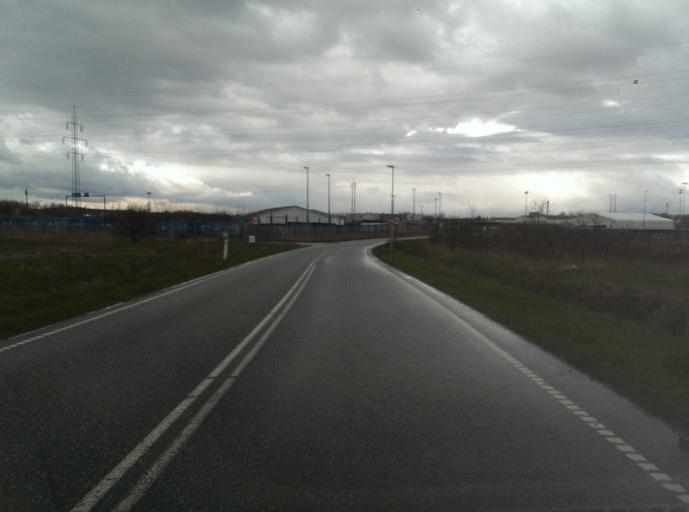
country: DK
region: South Denmark
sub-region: Esbjerg Kommune
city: Esbjerg
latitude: 55.4625
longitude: 8.5067
